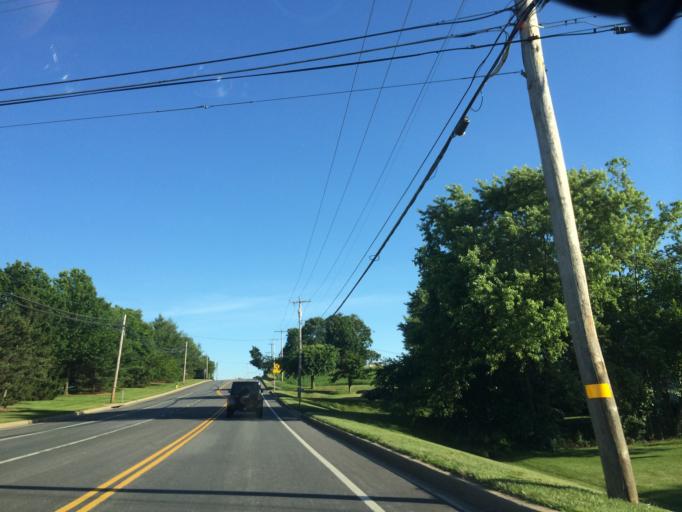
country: US
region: Maryland
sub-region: Carroll County
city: Westminster
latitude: 39.5326
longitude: -76.9944
